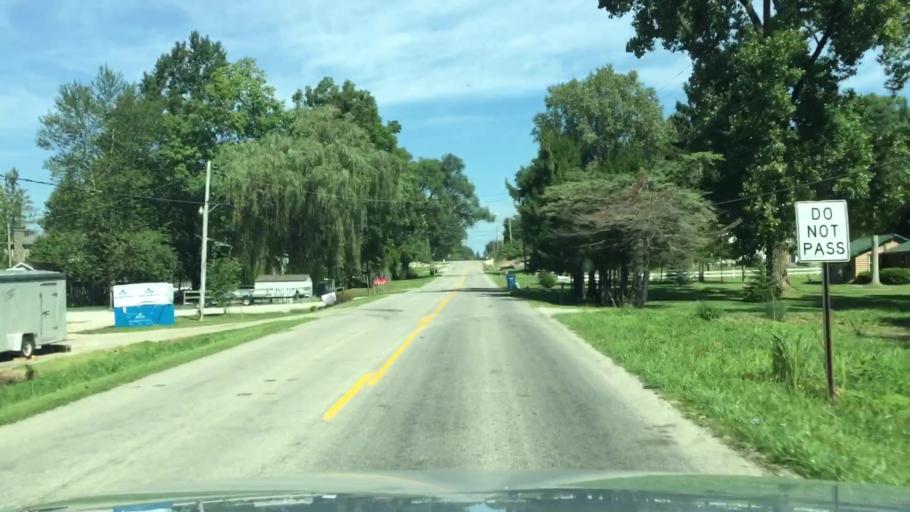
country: US
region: Michigan
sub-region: Lenawee County
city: Manitou Beach-Devils Lake
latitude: 41.9938
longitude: -84.2807
